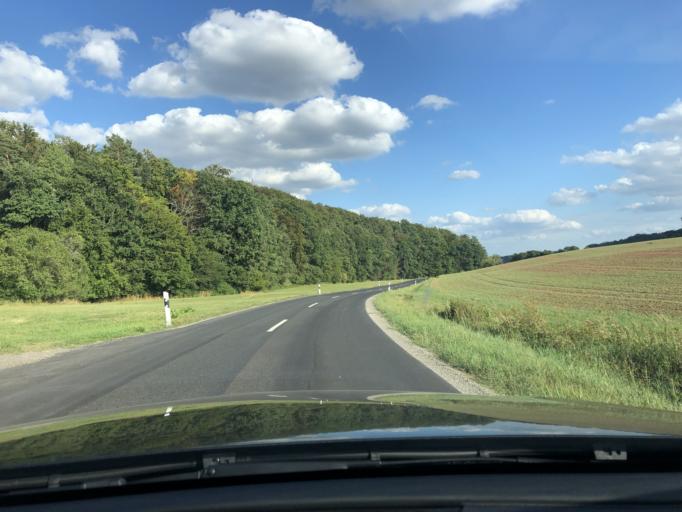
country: DE
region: Bavaria
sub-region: Regierungsbezirk Unterfranken
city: Kirchlauter
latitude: 50.0599
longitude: 10.6830
